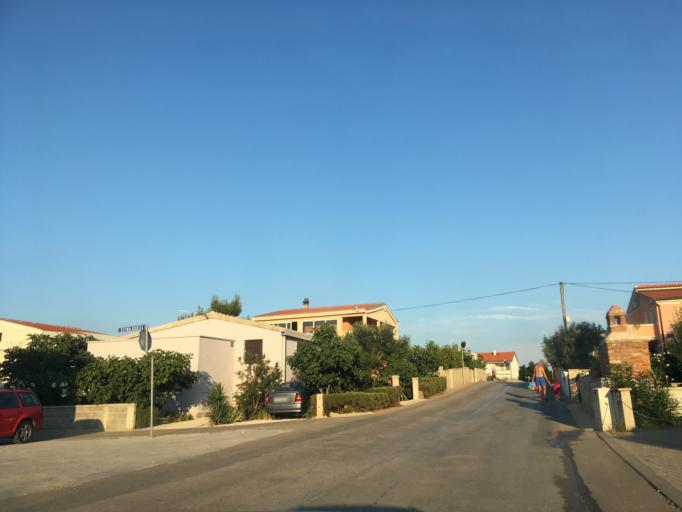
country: HR
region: Zadarska
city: Vir
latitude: 44.3051
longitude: 15.1026
